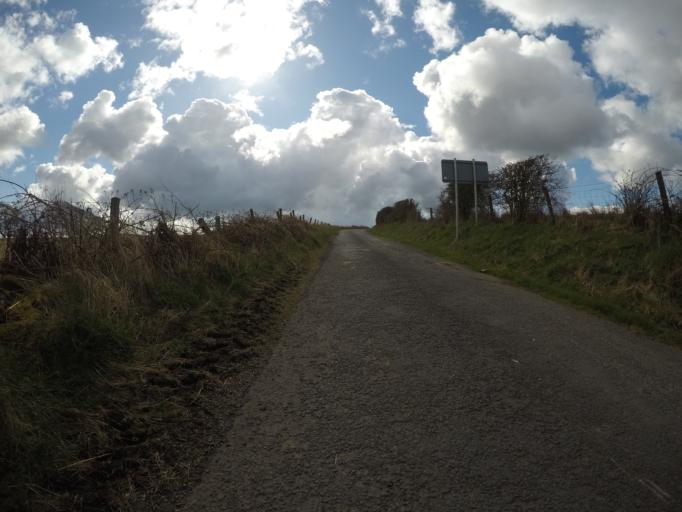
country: GB
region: Scotland
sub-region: North Ayrshire
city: Kilbirnie
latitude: 55.7250
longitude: -4.6660
